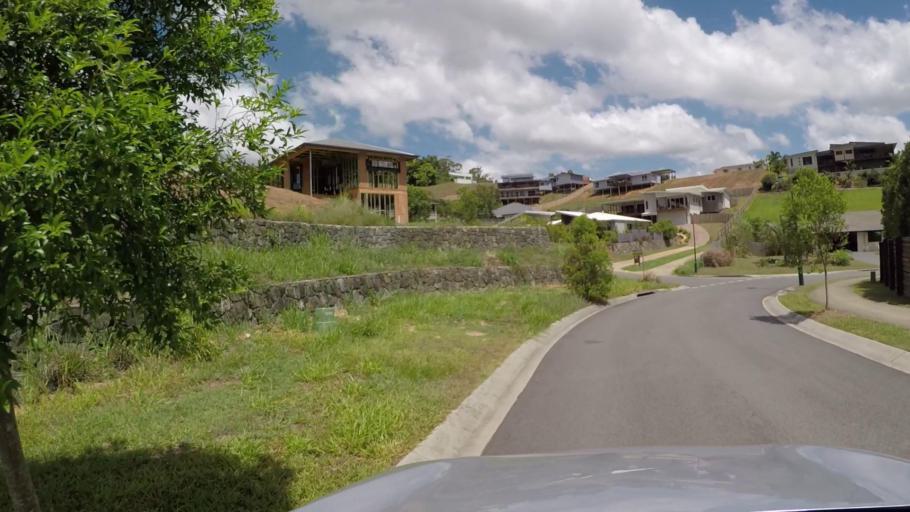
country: AU
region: Queensland
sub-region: Sunshine Coast
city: Woombye
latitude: -26.6692
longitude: 152.9720
